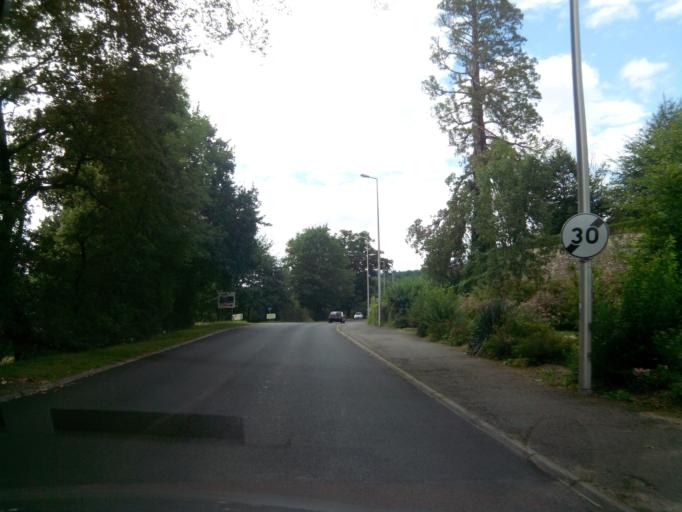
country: FR
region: Limousin
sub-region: Departement de la Haute-Vienne
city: Eymoutiers
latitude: 45.7394
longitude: 1.7383
